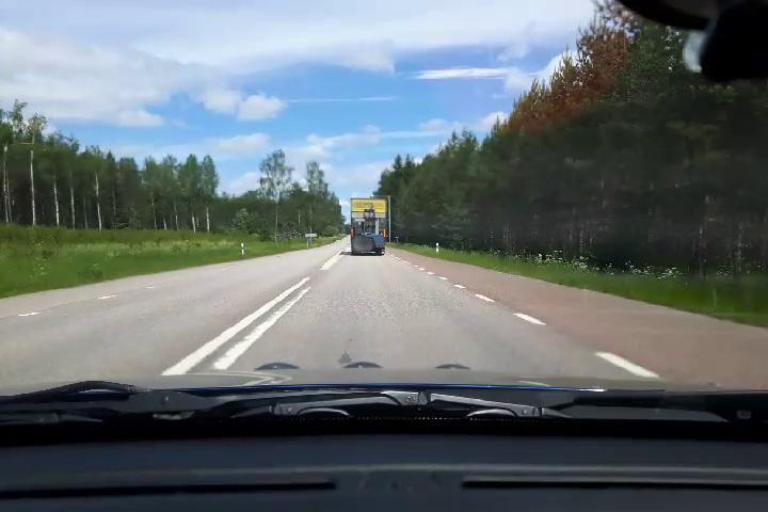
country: SE
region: Uppsala
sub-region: Osthammars Kommun
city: Bjorklinge
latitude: 60.0827
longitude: 17.5465
